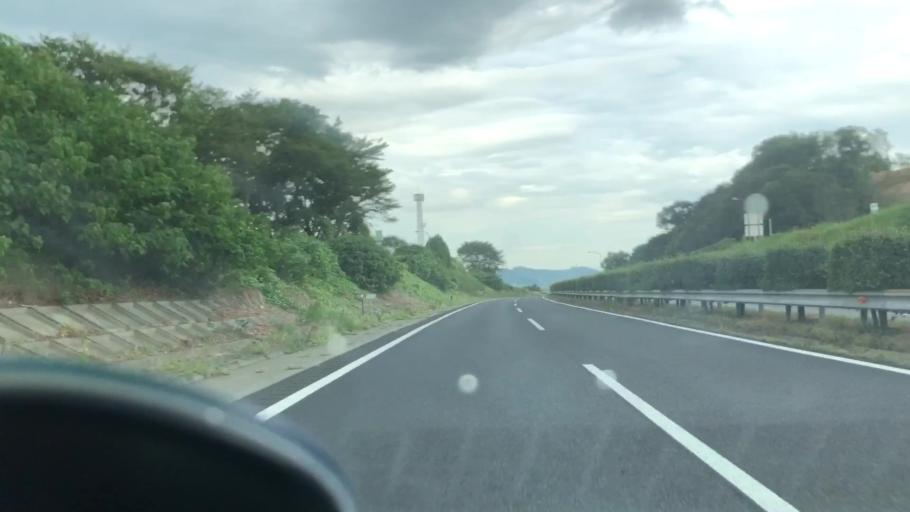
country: JP
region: Hyogo
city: Himeji
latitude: 34.9474
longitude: 134.8003
